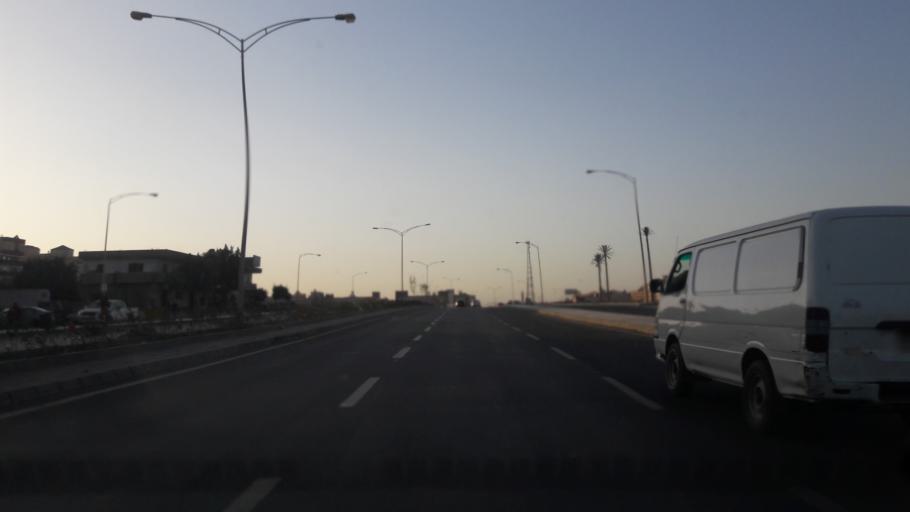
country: EG
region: Al Jizah
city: Madinat Sittah Uktubar
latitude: 29.9536
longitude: 30.9352
